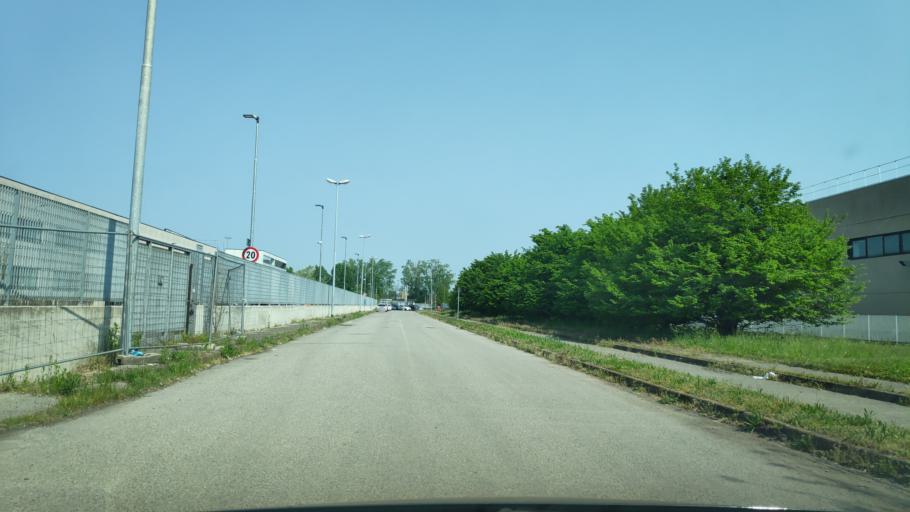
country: IT
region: Lombardy
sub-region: Citta metropolitana di Milano
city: Liscate
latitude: 45.4797
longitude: 9.3961
